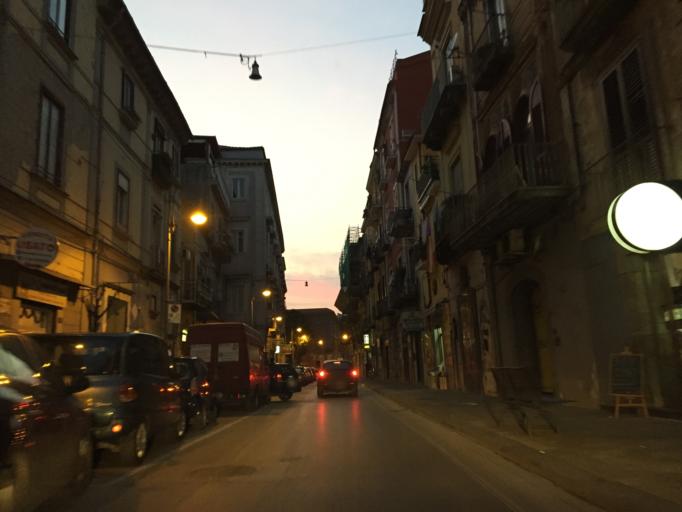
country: IT
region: Campania
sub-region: Provincia di Salerno
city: Nocera Inferiore
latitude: 40.7464
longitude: 14.6451
